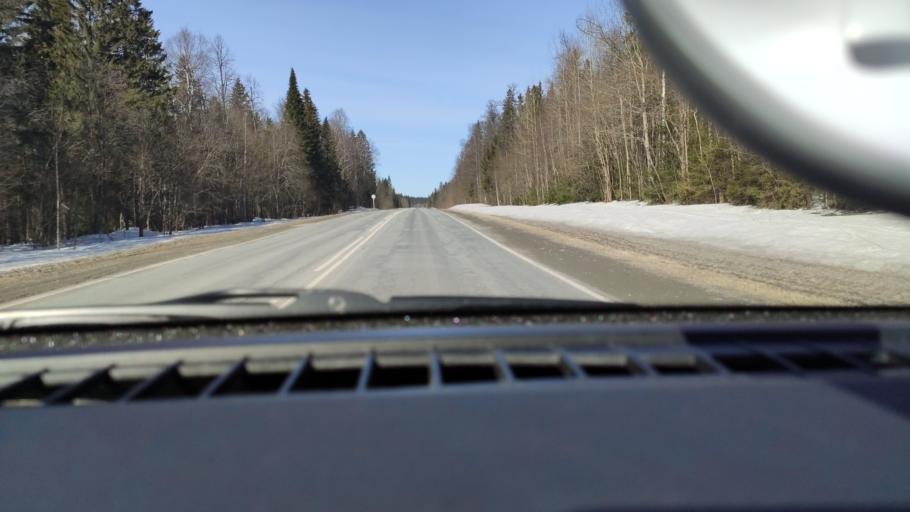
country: RU
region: Perm
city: Perm
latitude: 58.1859
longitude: 56.2198
